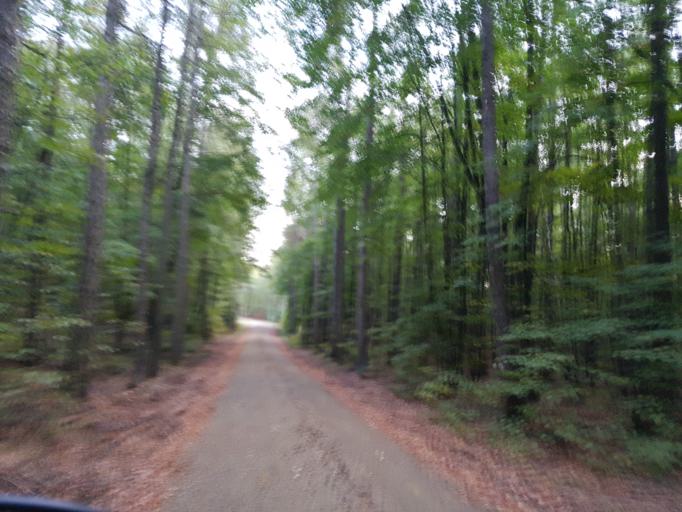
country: DE
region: Brandenburg
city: Trobitz
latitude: 51.5664
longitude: 13.4461
